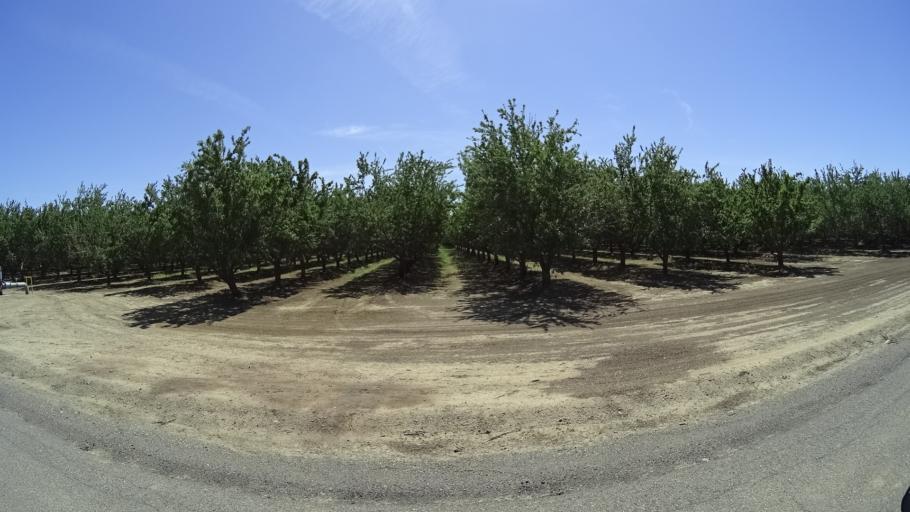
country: US
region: California
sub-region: Glenn County
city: Orland
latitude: 39.7323
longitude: -122.1236
